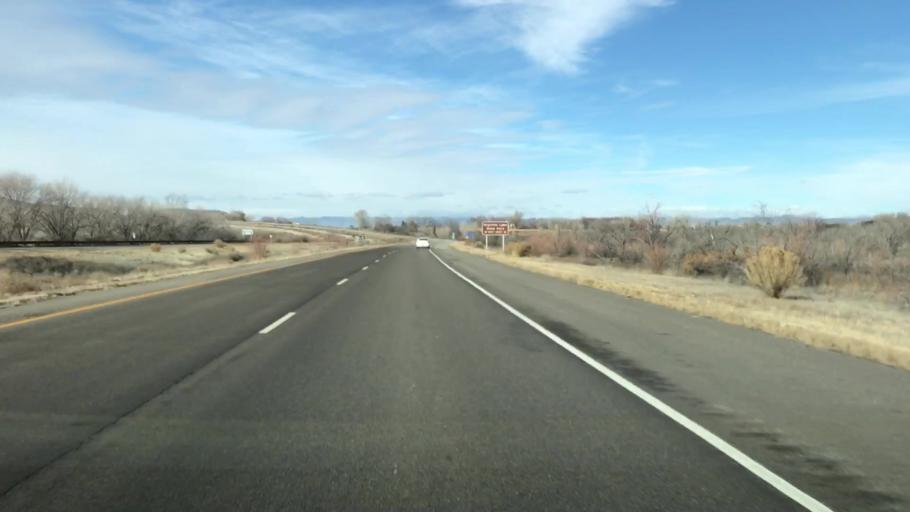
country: US
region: Colorado
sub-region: Mesa County
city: Loma
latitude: 39.1719
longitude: -108.7957
